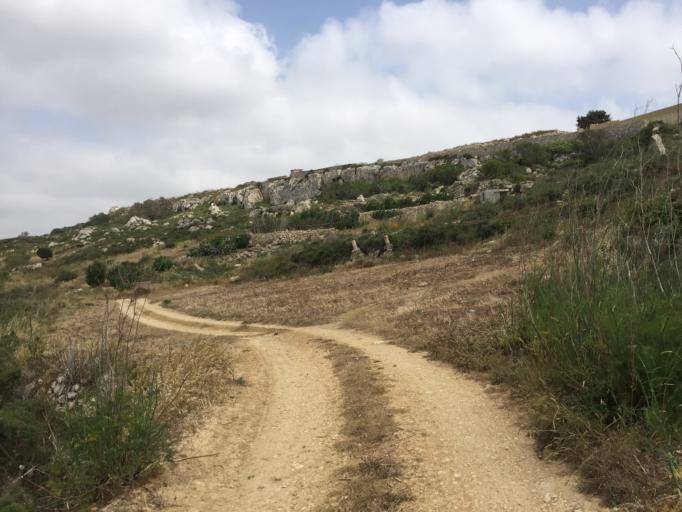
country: MT
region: L-Imgarr
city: Imgarr
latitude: 35.9025
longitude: 14.3476
